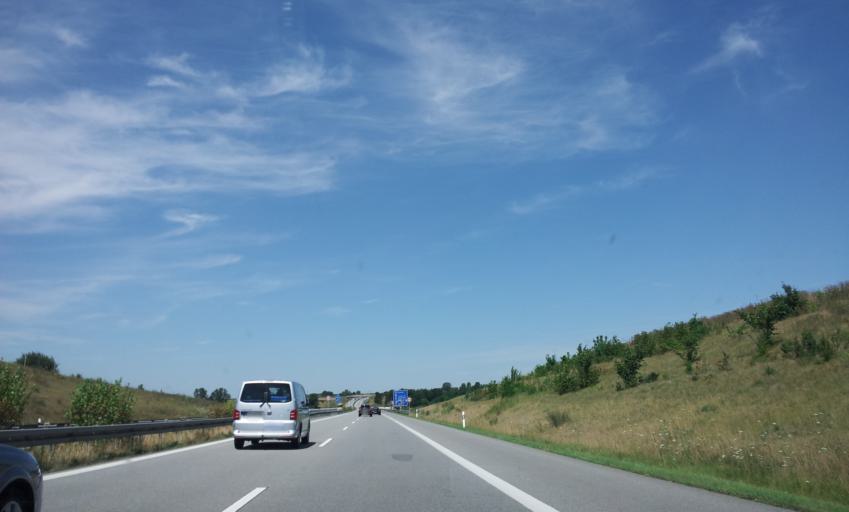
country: DE
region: Mecklenburg-Vorpommern
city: Kessin
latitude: 53.7803
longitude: 13.3278
